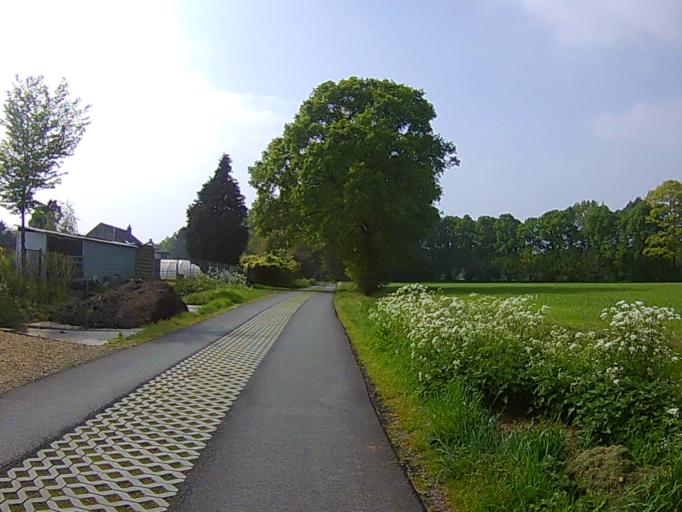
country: BE
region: Flanders
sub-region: Provincie Antwerpen
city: Grobbendonk
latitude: 51.2091
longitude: 4.7208
